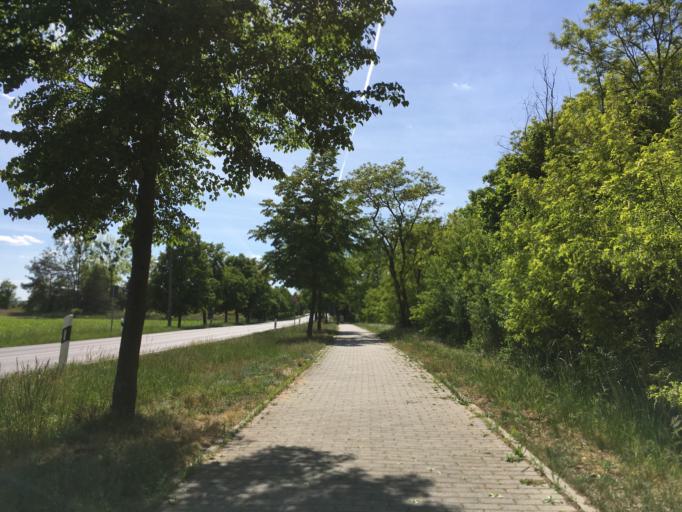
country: DE
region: Brandenburg
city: Oderberg
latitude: 52.8382
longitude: 14.1039
